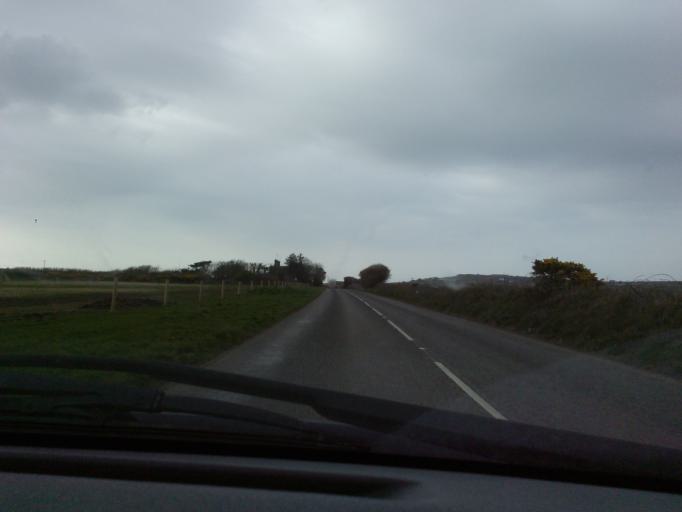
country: GB
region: England
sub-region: Cornwall
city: Saint Just
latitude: 50.1055
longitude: -5.6705
